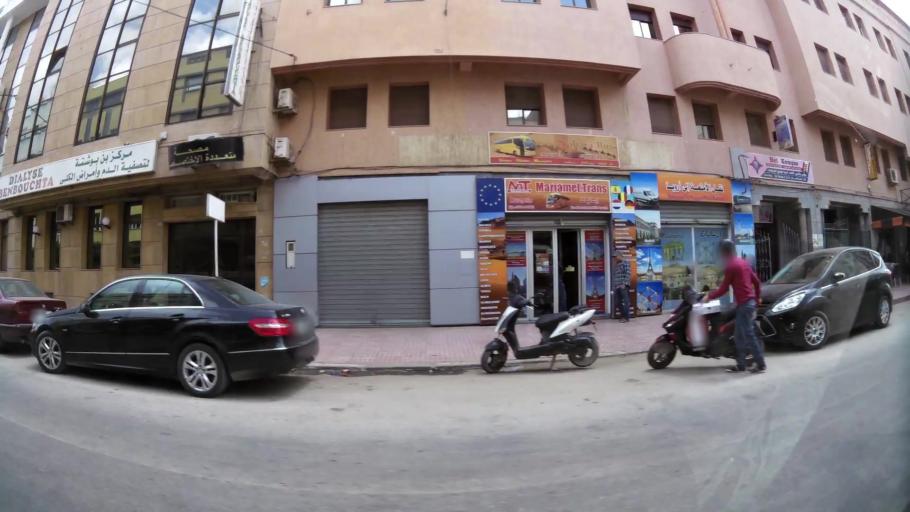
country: MA
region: Oriental
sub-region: Nador
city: Nador
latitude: 35.1711
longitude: -2.9199
